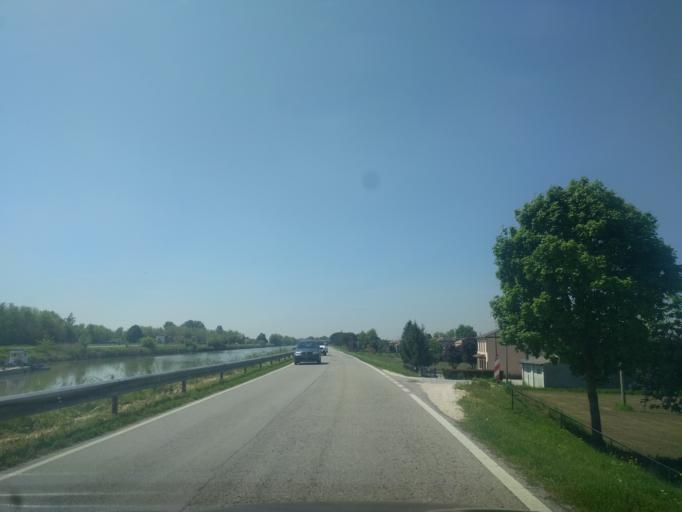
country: IT
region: Veneto
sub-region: Provincia di Rovigo
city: Villanova Marchesana
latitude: 45.0501
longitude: 11.9860
